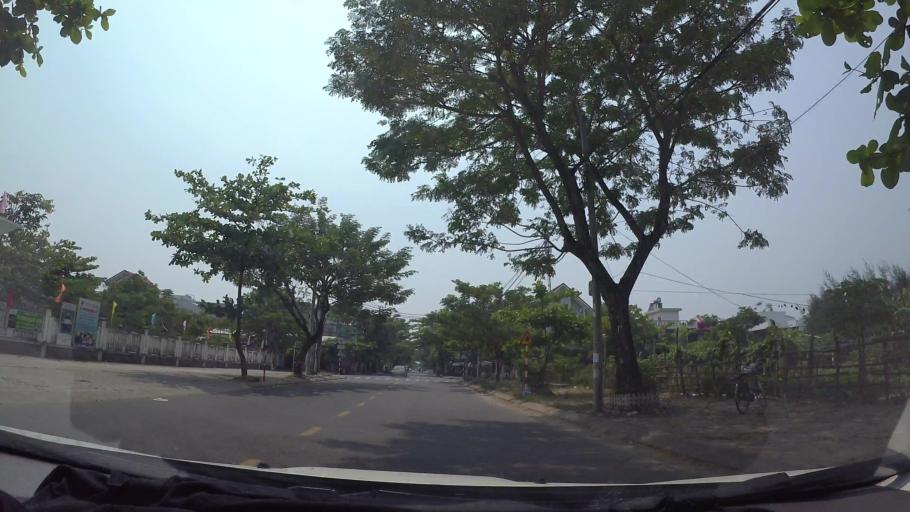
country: VN
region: Da Nang
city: Cam Le
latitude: 16.0026
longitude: 108.2130
